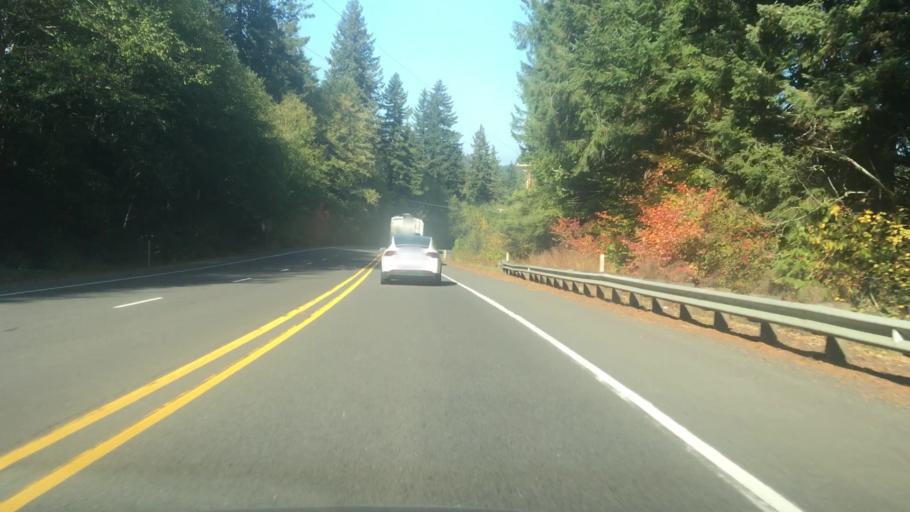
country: US
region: Oregon
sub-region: Polk County
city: Grand Ronde
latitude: 45.0658
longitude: -123.7288
